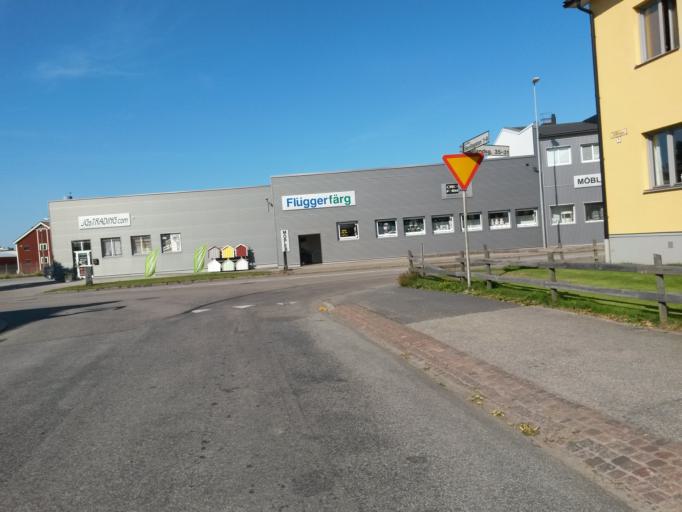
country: SE
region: Vaestra Goetaland
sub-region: Lidkopings Kommun
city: Lidkoping
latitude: 58.5068
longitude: 13.1538
